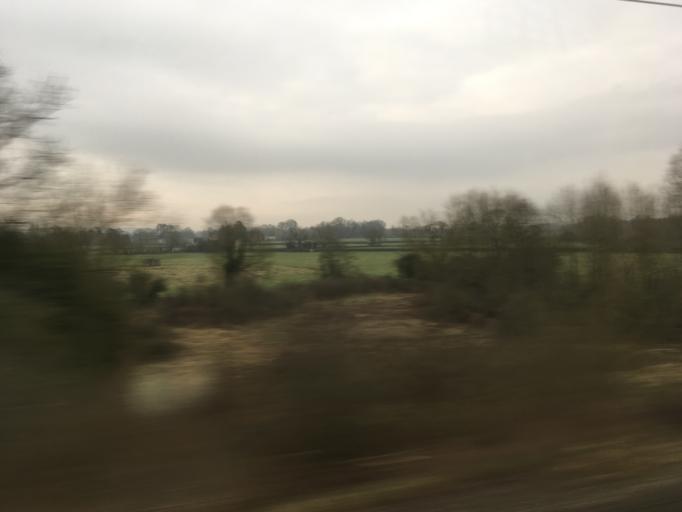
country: GB
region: England
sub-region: Wiltshire
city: Charlton
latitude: 51.5566
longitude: -2.0296
